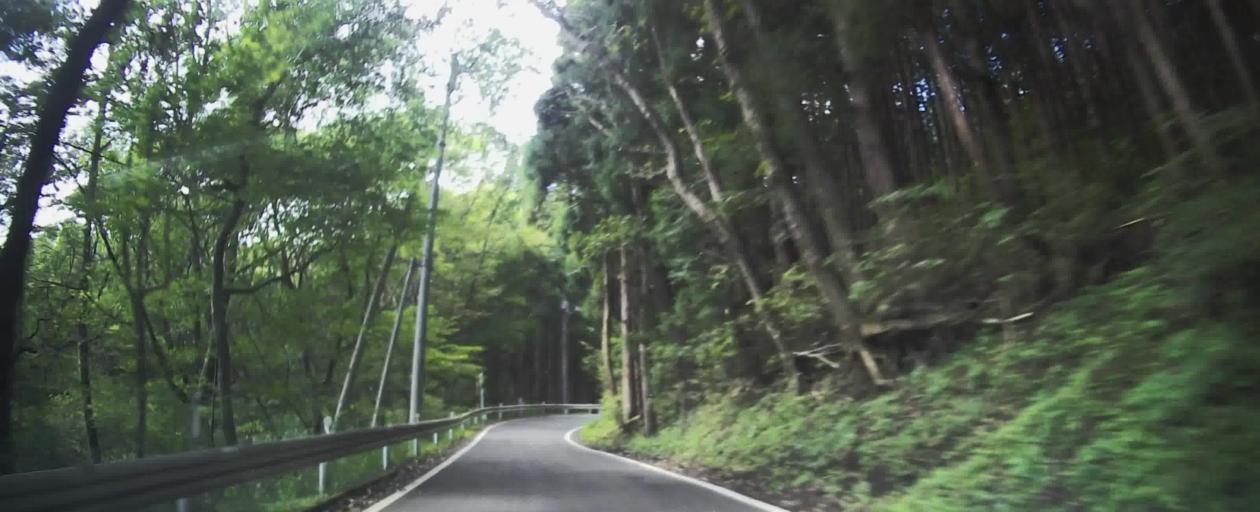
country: JP
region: Gunma
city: Kanekomachi
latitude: 36.4502
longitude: 138.9038
